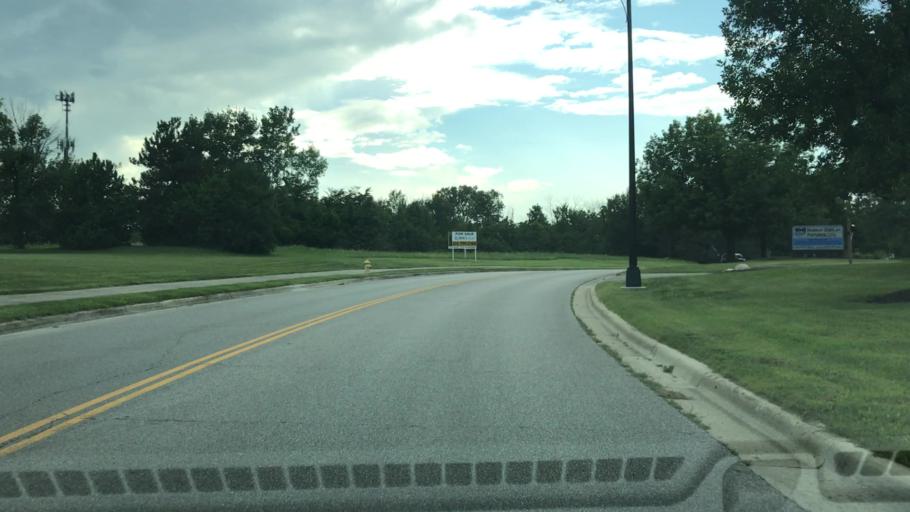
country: US
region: Ohio
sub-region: Franklin County
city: Grove City
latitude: 39.8874
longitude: -83.0649
